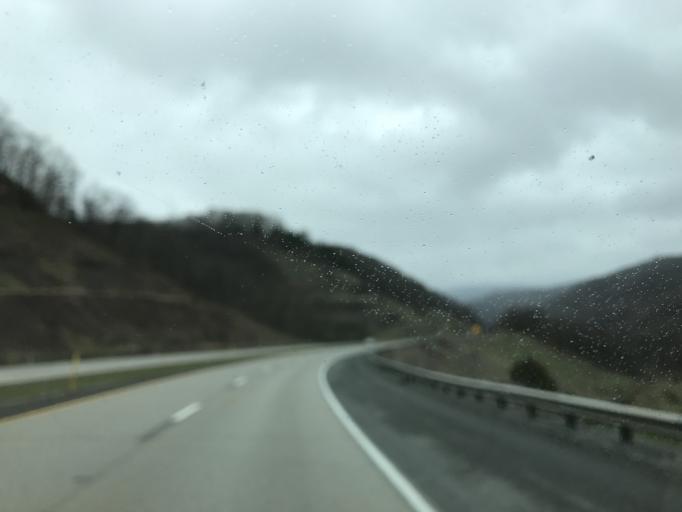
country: US
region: West Virginia
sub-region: Summers County
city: Hinton
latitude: 37.7826
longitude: -80.9661
